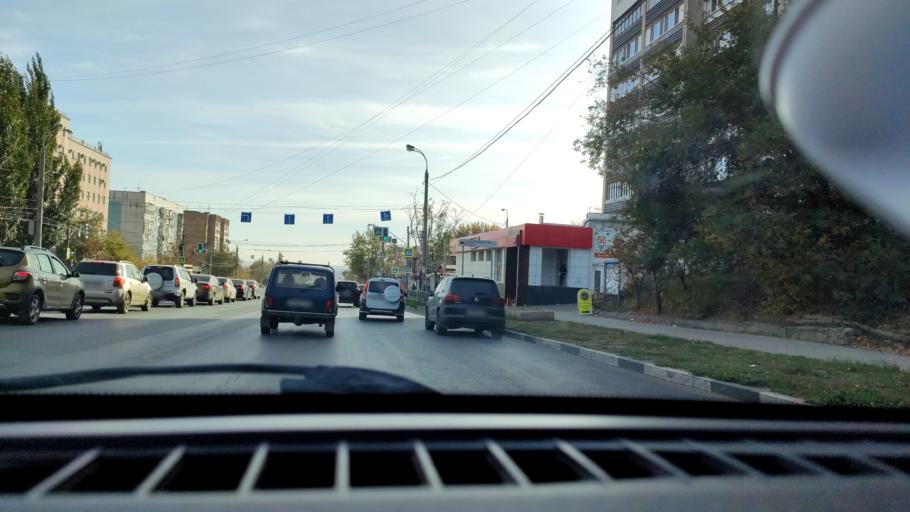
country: RU
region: Samara
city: Samara
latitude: 53.1883
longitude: 50.1911
